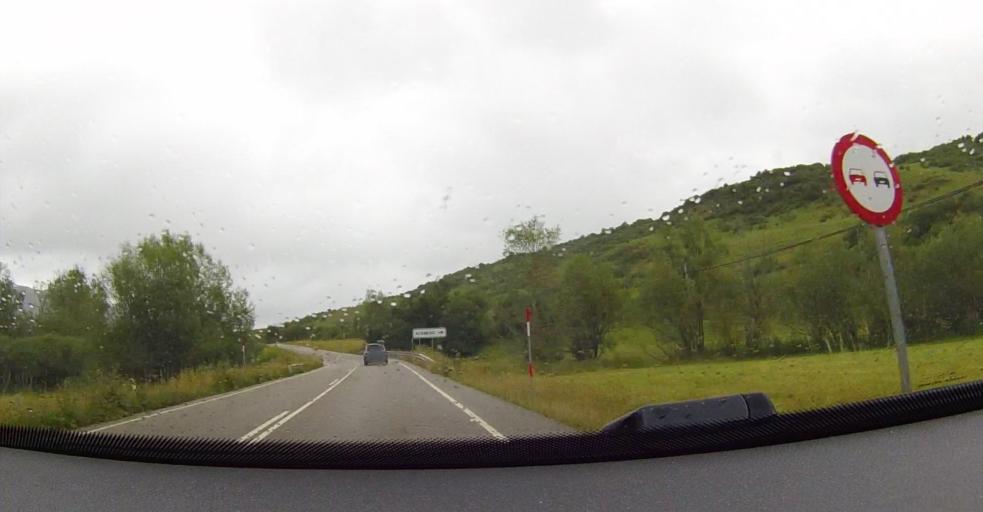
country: ES
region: Castille and Leon
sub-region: Provincia de Leon
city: Acebedo
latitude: 43.0451
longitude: -5.1245
